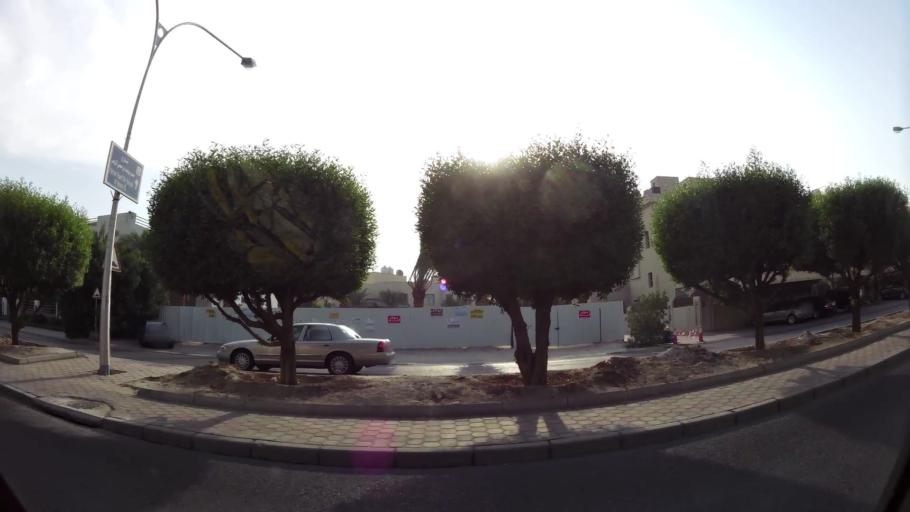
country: KW
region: Muhafazat Hawalli
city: Hawalli
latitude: 29.3107
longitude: 48.0077
